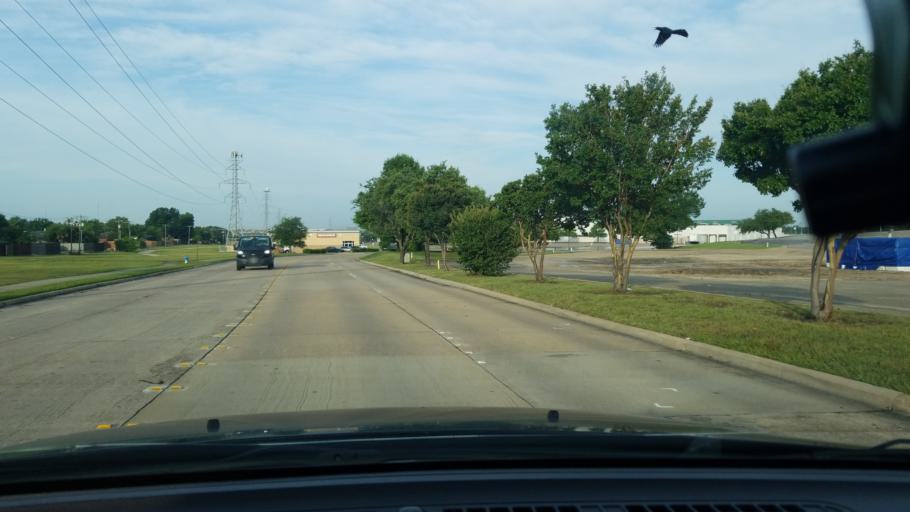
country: US
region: Texas
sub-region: Dallas County
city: Mesquite
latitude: 32.8056
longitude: -96.6200
